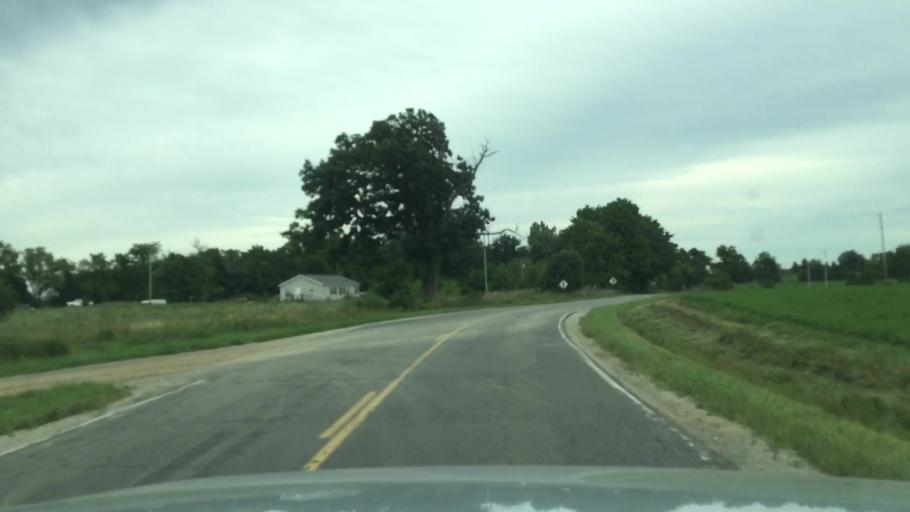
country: US
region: Michigan
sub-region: Shiawassee County
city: Durand
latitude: 42.8622
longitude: -84.0435
